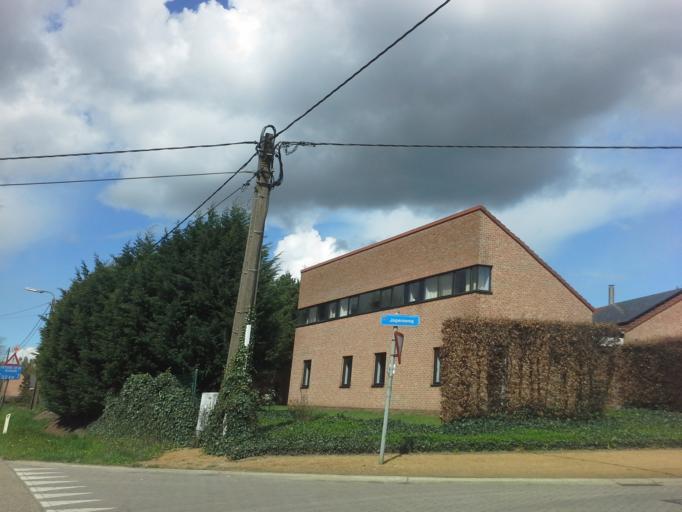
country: BE
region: Flanders
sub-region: Provincie Antwerpen
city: Meerhout
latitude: 51.1228
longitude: 5.0470
